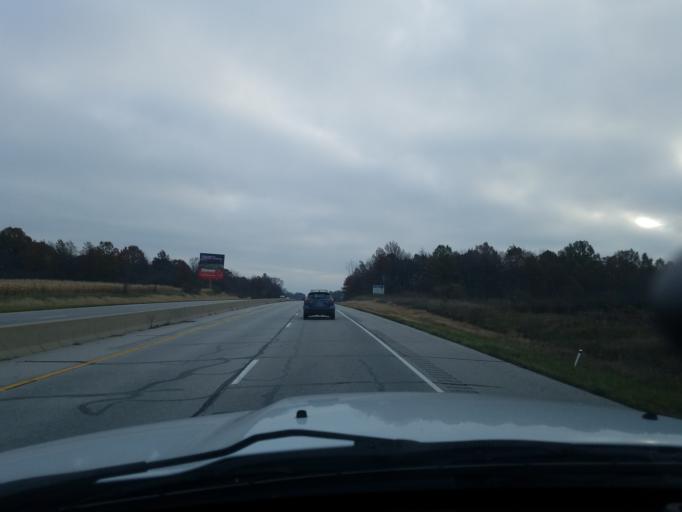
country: US
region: Indiana
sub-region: Delaware County
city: Yorktown
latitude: 40.2191
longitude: -85.5139
